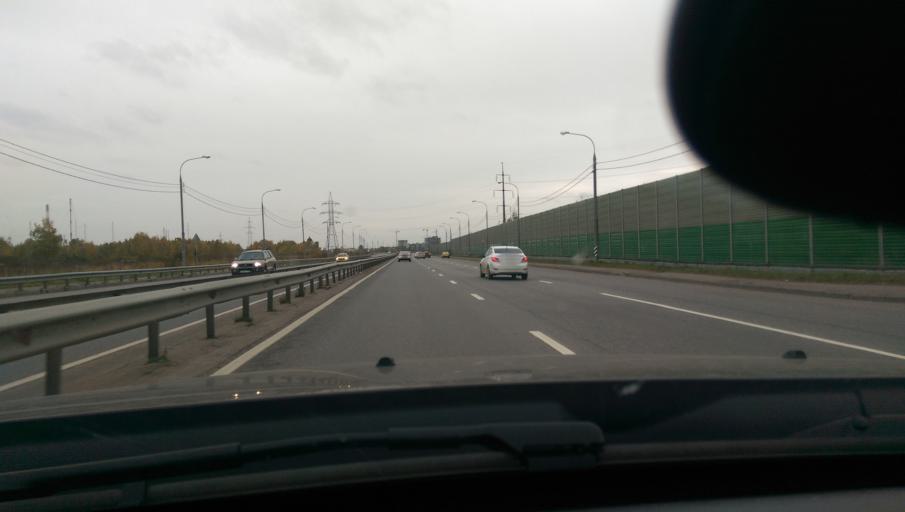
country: RU
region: Moscow
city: Vatutino
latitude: 55.9372
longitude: 37.6563
